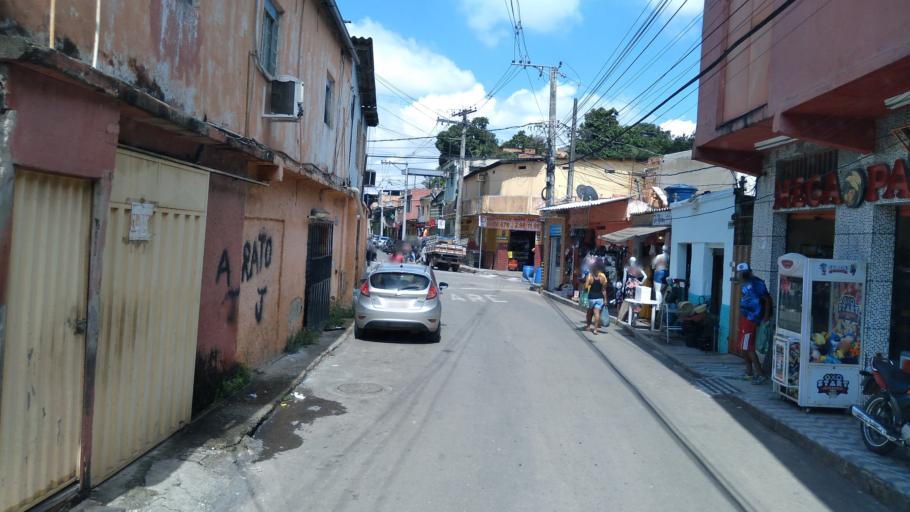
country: BR
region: Minas Gerais
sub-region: Santa Luzia
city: Santa Luzia
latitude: -19.8323
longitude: -43.8908
